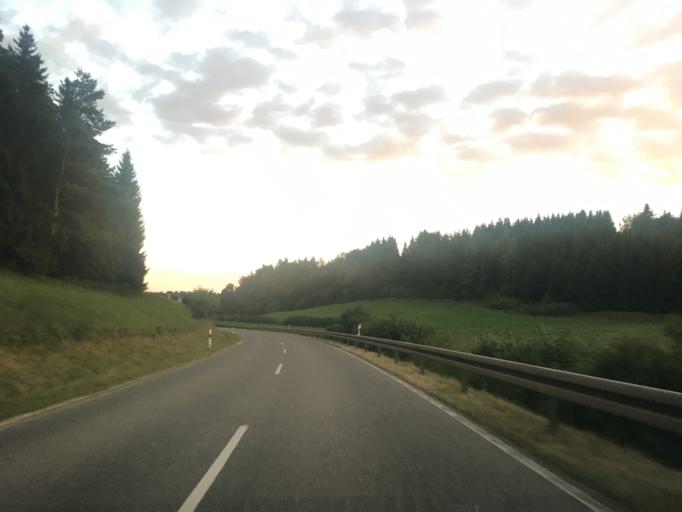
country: DE
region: Baden-Wuerttemberg
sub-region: Tuebingen Region
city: Hayingen
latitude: 48.3312
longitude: 9.4331
